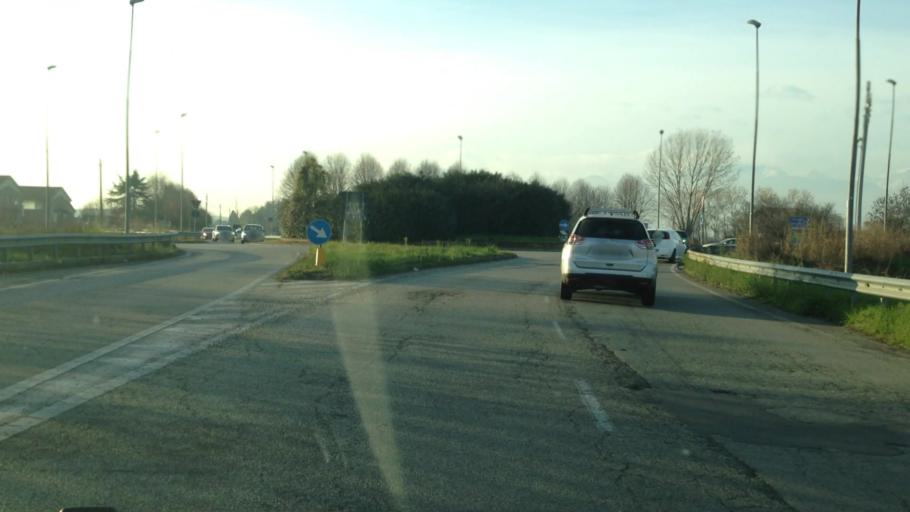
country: IT
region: Piedmont
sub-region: Provincia di Torino
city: Collegno
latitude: 45.0963
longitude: 7.5903
